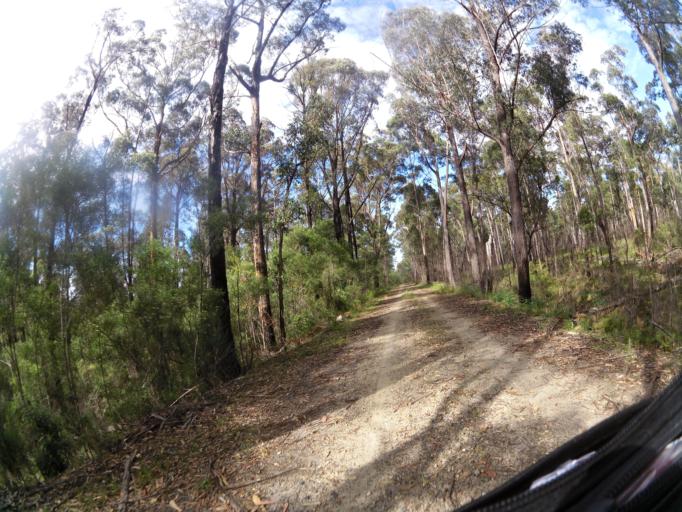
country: AU
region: Victoria
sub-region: East Gippsland
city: Lakes Entrance
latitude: -37.7503
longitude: 148.2172
